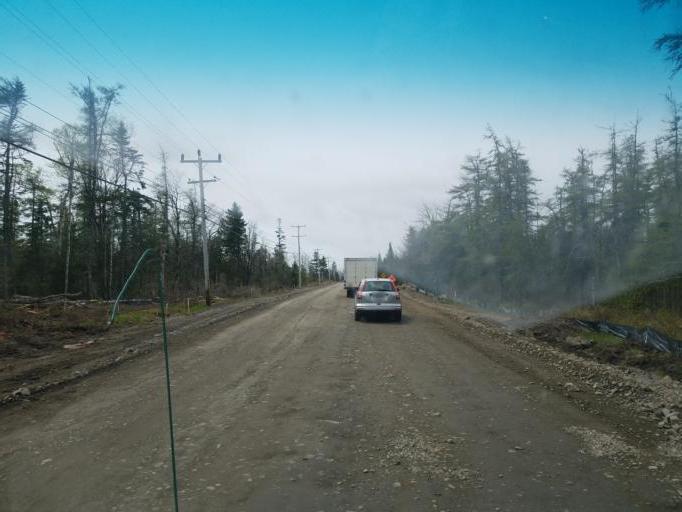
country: US
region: Maine
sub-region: Washington County
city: East Machias
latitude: 44.7718
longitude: -67.1971
